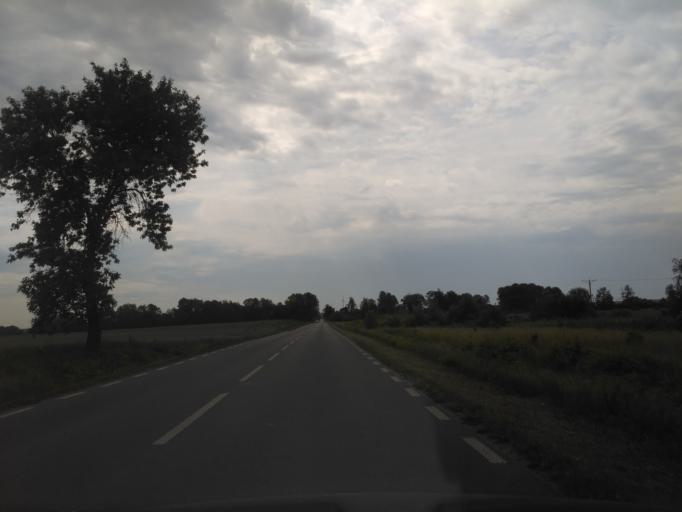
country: PL
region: Lublin Voivodeship
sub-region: Powiat chelmski
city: Pokrowka
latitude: 51.0828
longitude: 23.5129
